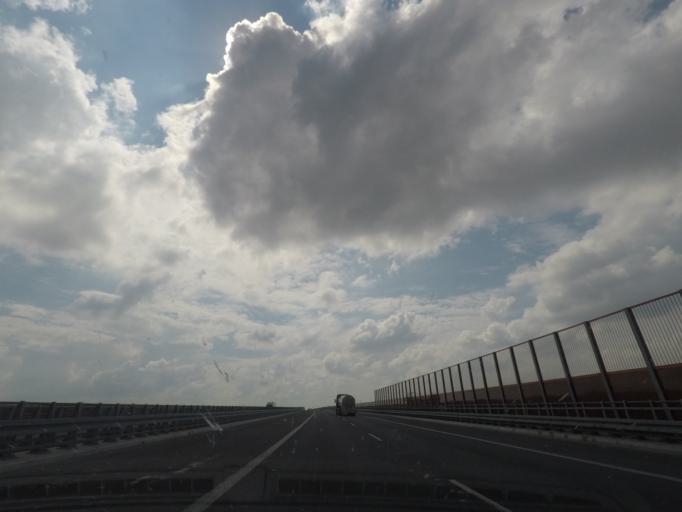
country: PL
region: Lodz Voivodeship
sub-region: Powiat kutnowski
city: Krzyzanow
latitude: 52.1377
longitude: 19.4842
